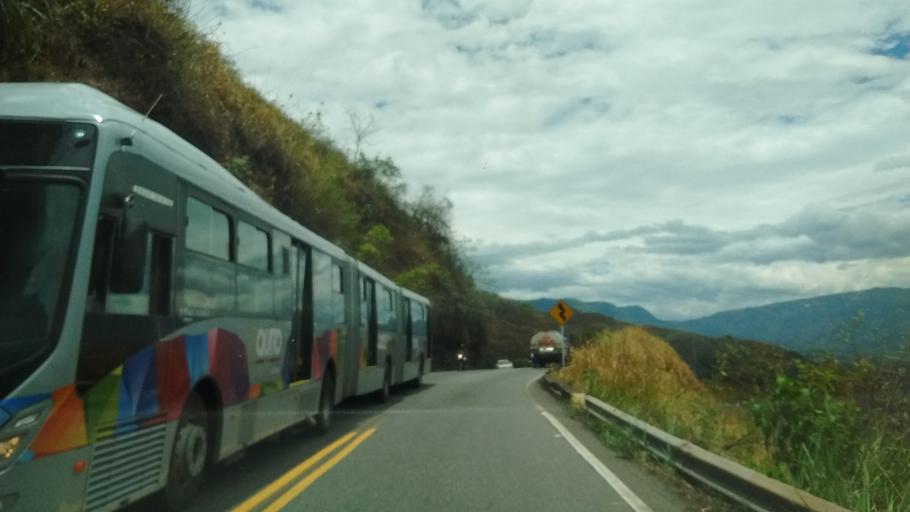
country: CO
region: Cauca
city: La Sierra
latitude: 2.1938
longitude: -76.8353
